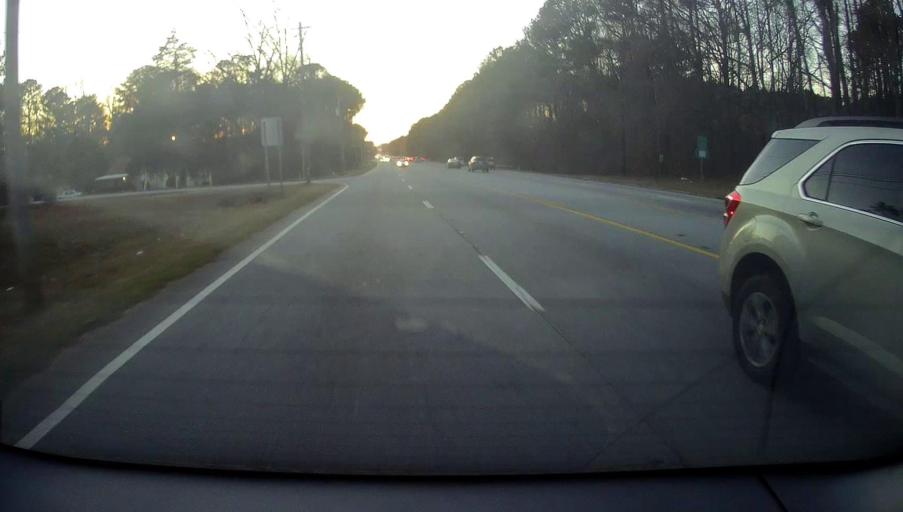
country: US
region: Georgia
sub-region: Clayton County
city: Riverdale
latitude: 33.5503
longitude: -84.4218
